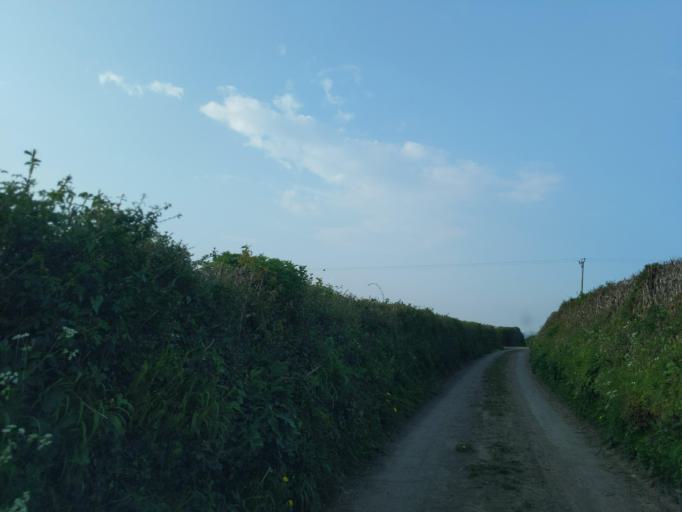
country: GB
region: England
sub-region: Devon
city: Plympton
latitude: 50.3567
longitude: -4.0387
